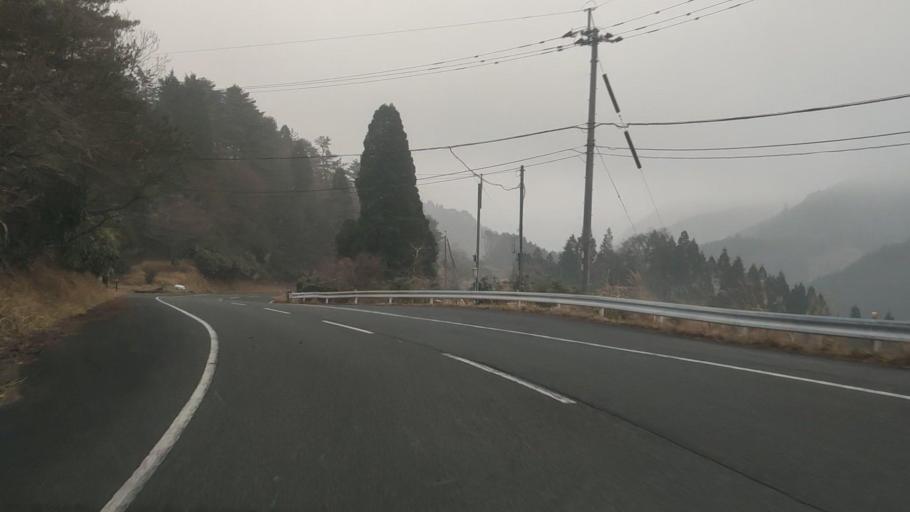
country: JP
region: Kumamoto
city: Matsubase
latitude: 32.5723
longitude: 130.9062
